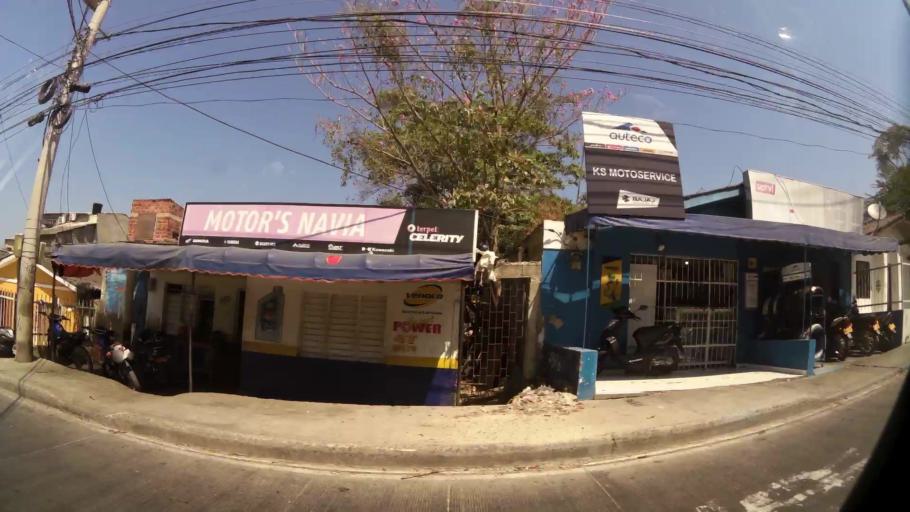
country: CO
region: Bolivar
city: Cartagena
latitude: 10.4050
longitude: -75.4845
